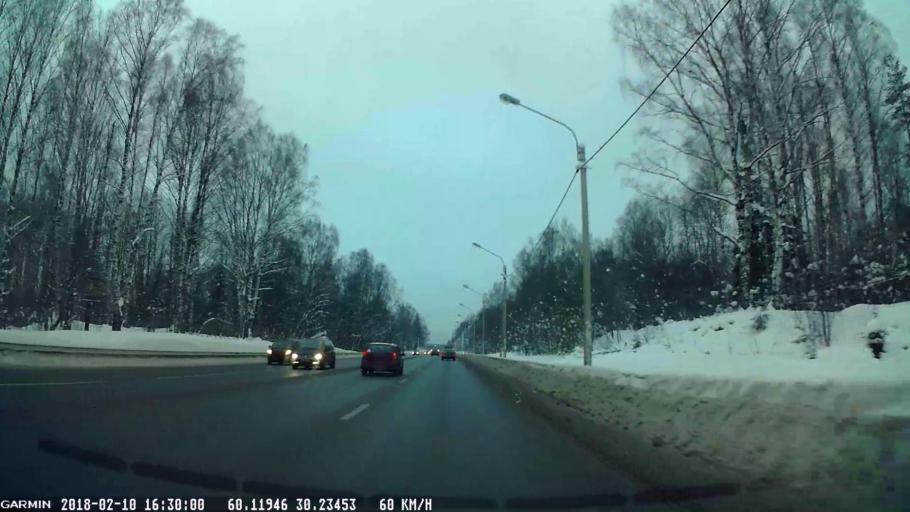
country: RU
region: St.-Petersburg
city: Levashovo
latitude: 60.1200
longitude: 30.2340
